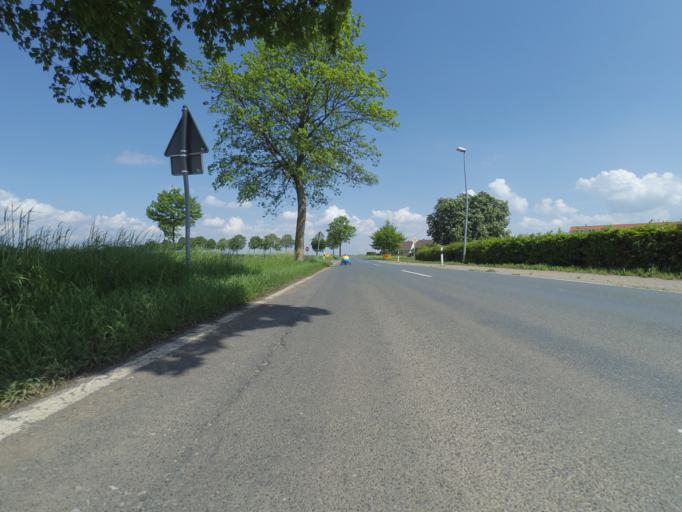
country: DE
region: Lower Saxony
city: Hohenhameln
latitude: 52.2049
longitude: 10.0356
